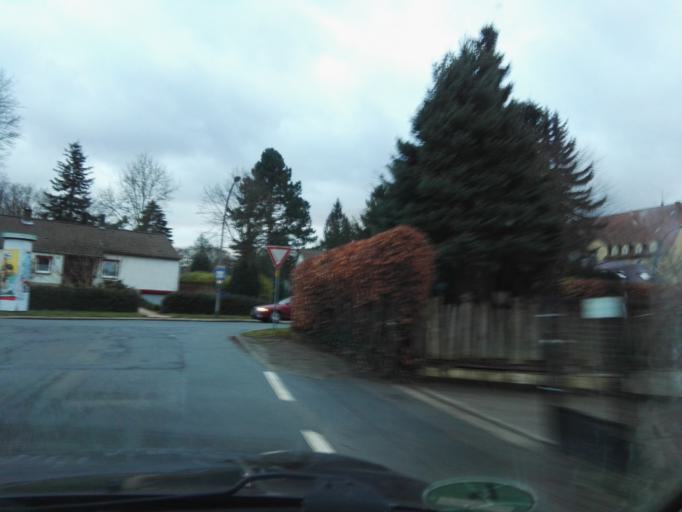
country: DE
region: Lower Saxony
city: Leiferde
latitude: 52.1947
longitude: 10.4752
